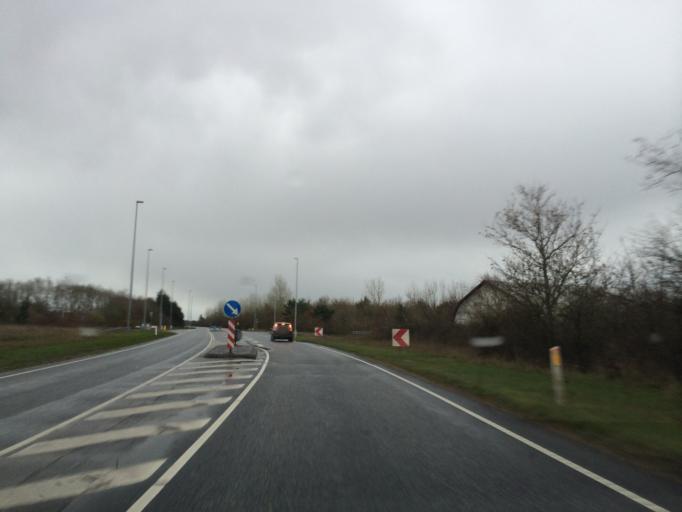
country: DK
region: Central Jutland
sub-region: Ringkobing-Skjern Kommune
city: Tarm
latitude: 55.9042
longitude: 8.5039
